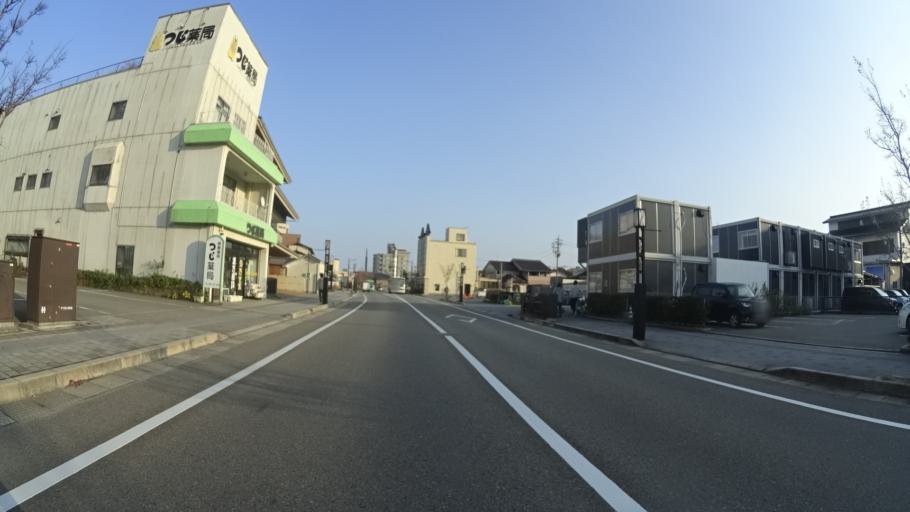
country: JP
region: Ishikawa
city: Nanao
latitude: 37.0893
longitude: 136.9167
